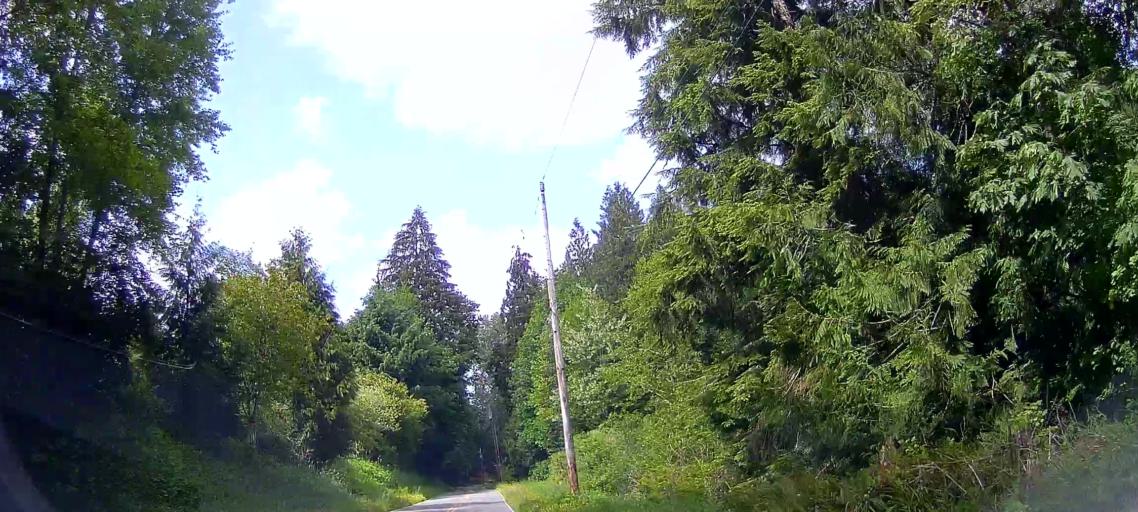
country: US
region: Washington
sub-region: Whatcom County
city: Sudden Valley
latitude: 48.6617
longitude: -122.1972
